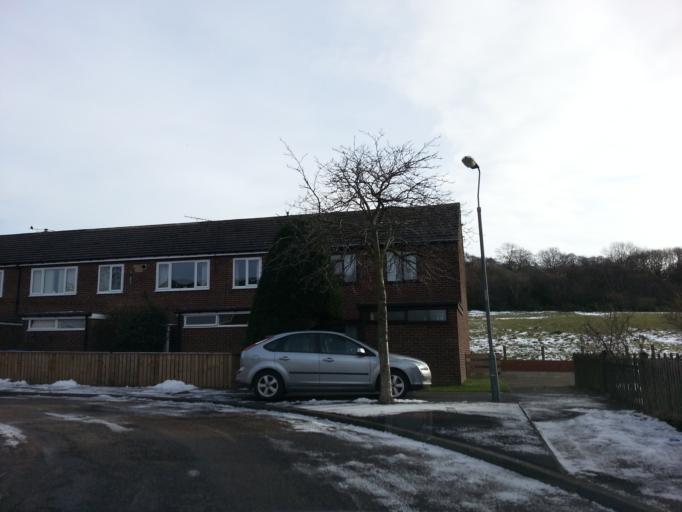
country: GB
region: England
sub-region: County Durham
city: Crook
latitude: 54.7064
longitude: -1.7422
